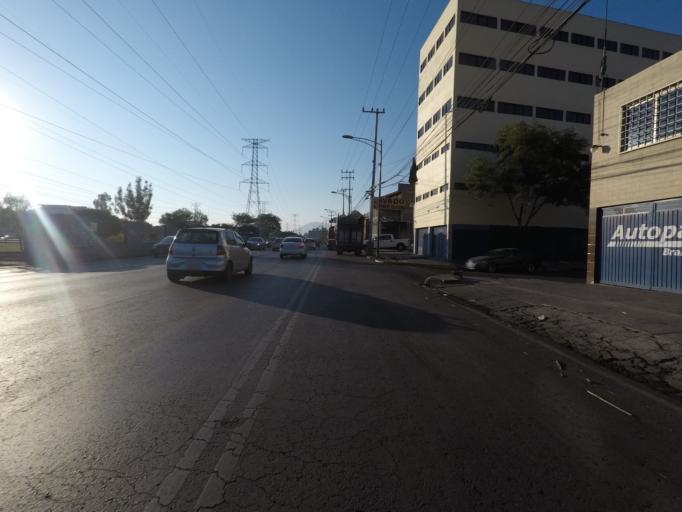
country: MX
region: Mexico City
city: Iztapalapa
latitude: 19.3675
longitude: -99.0735
